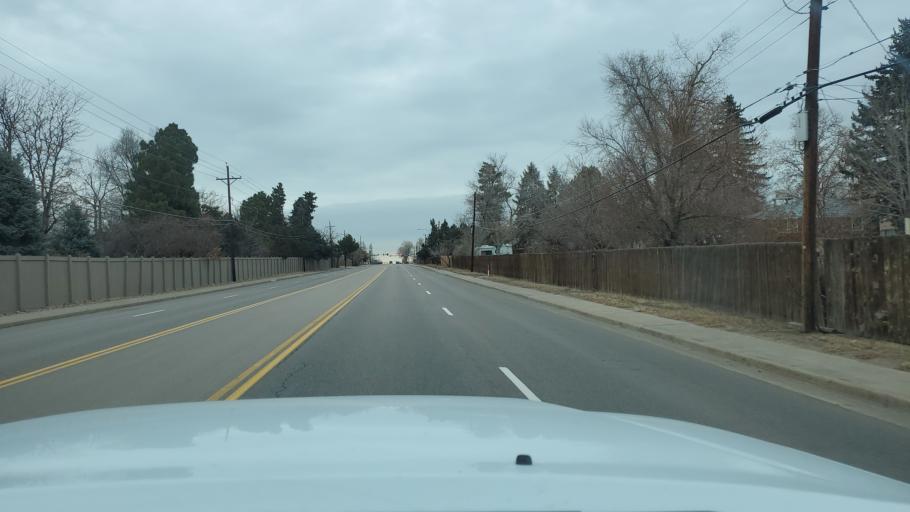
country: US
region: Colorado
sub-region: Arapahoe County
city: Southglenn
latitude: 39.5911
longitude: -104.9414
